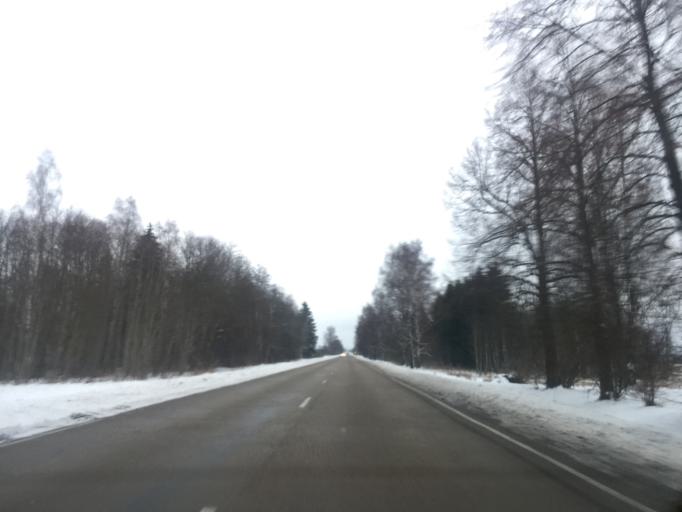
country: LV
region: Karsava
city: Karsava
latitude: 56.7860
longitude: 27.7060
